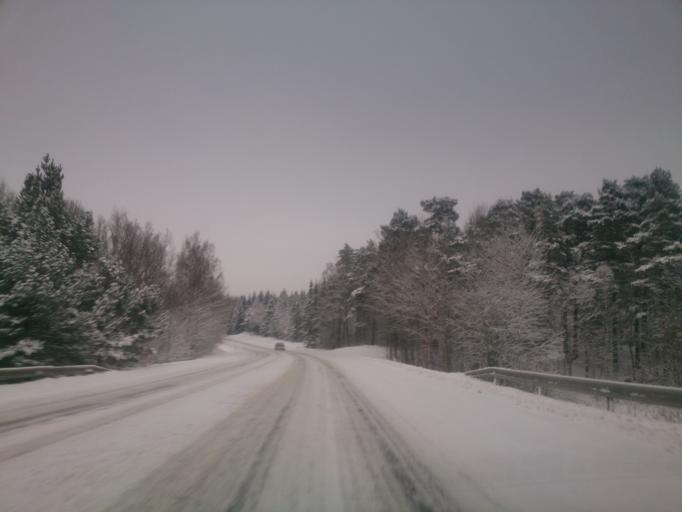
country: SE
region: OEstergoetland
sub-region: Norrkopings Kommun
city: Kimstad
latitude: 58.5031
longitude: 15.9777
